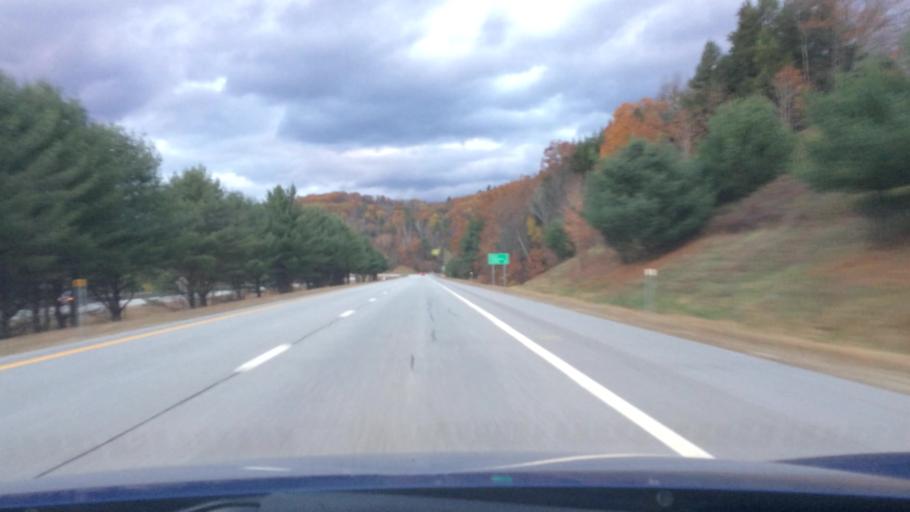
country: US
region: New Hampshire
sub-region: Grafton County
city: Woodstock
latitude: 43.9661
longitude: -71.6762
